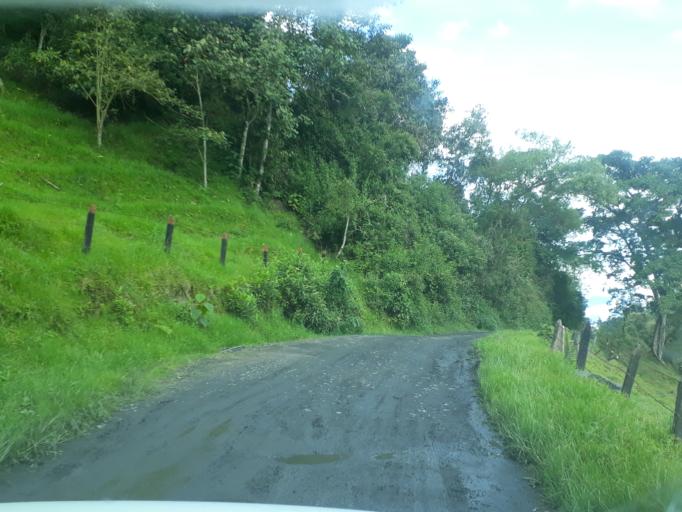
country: CO
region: Cundinamarca
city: Carmen de Carupa
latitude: 5.3437
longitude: -74.0529
